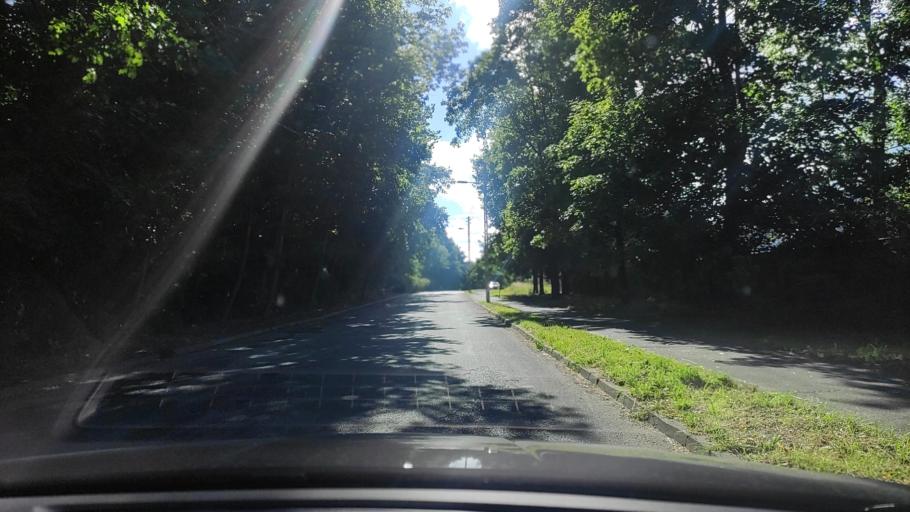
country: PL
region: Greater Poland Voivodeship
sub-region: Poznan
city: Poznan
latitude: 52.4055
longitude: 16.9874
